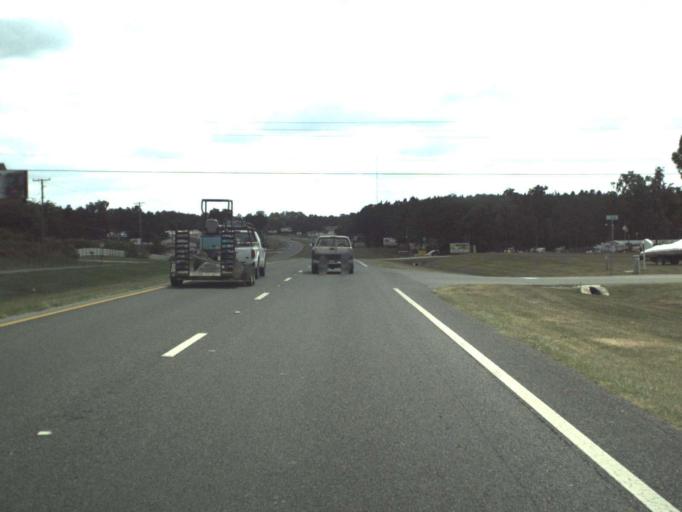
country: US
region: Florida
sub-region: Marion County
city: Ocala
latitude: 29.2463
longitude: -82.1523
